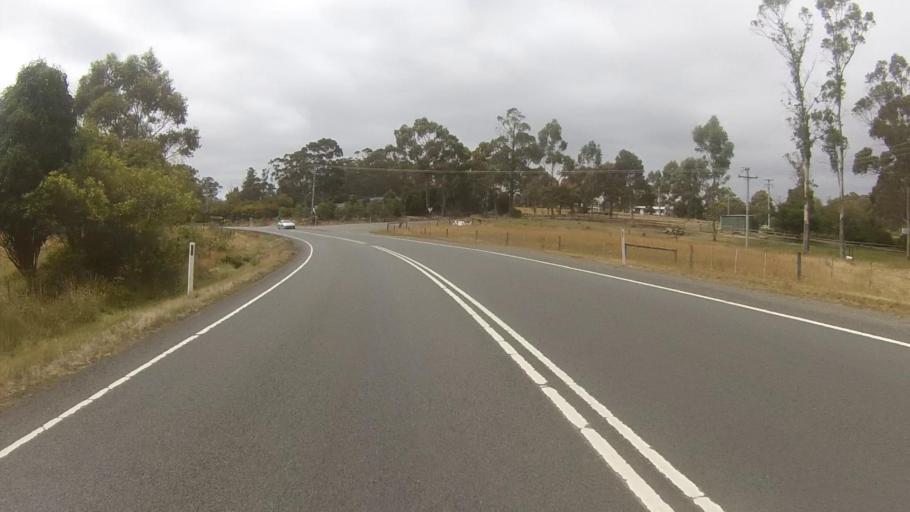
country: AU
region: Tasmania
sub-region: Kingborough
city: Margate
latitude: -42.9918
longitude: 147.1985
